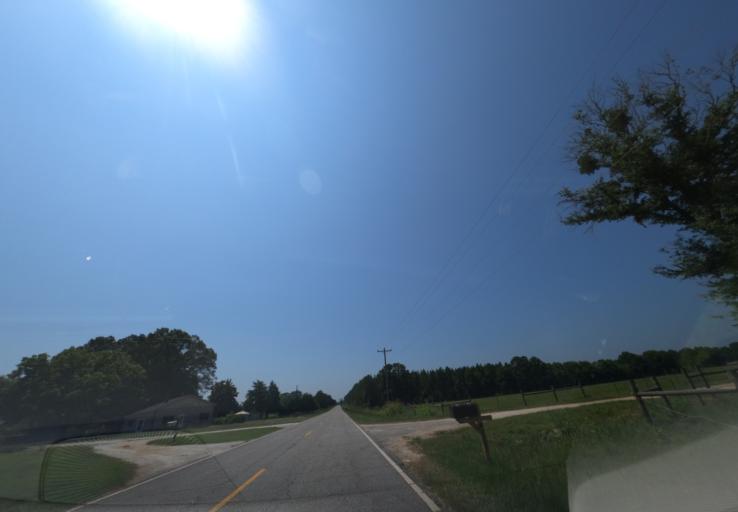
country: US
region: South Carolina
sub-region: Greenwood County
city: Greenwood
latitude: 34.0230
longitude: -82.1275
